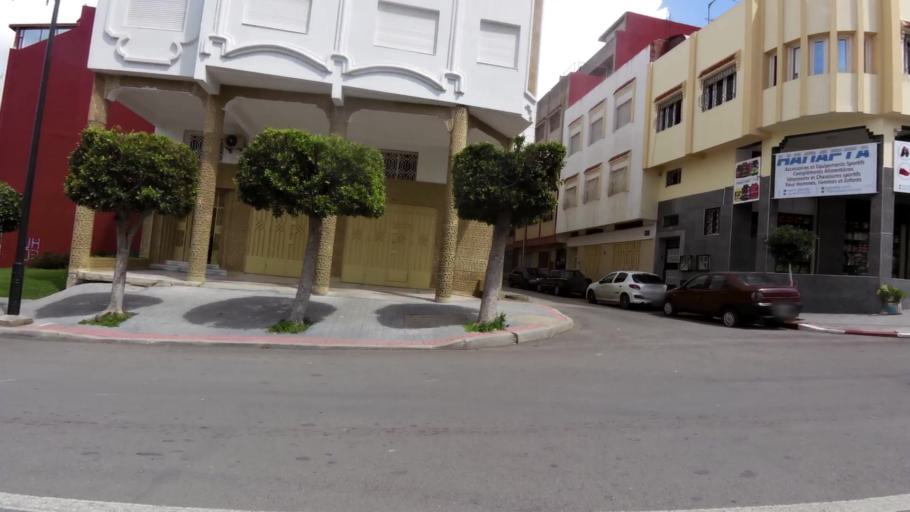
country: MA
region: Tanger-Tetouan
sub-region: Tanger-Assilah
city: Tangier
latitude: 35.7544
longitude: -5.8306
